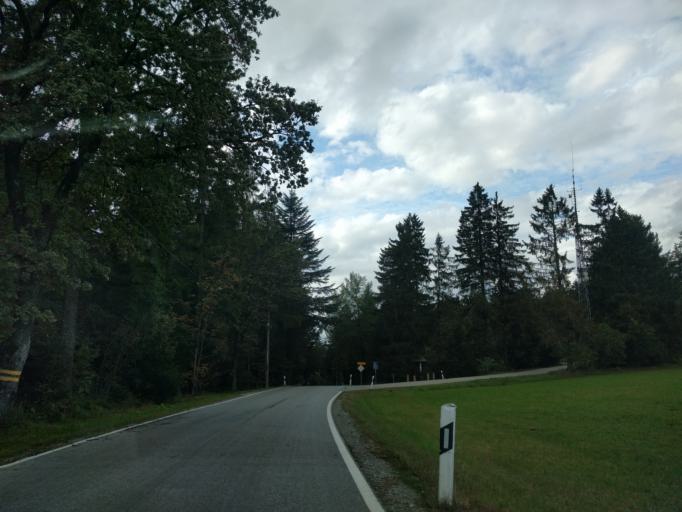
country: DE
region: Bavaria
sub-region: Lower Bavaria
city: Schaufling
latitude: 48.8746
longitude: 13.0239
